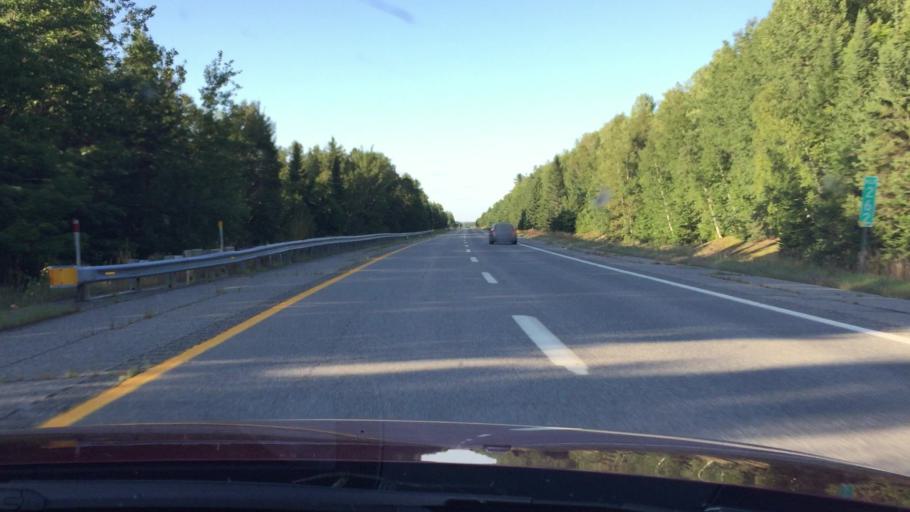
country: US
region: Maine
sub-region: Penobscot County
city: Patten
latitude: 45.8443
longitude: -68.4314
